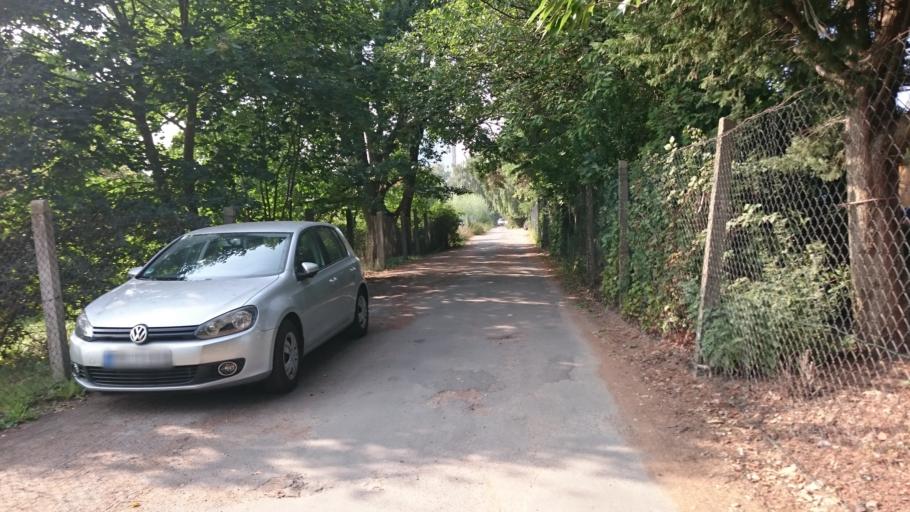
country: DE
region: Mecklenburg-Vorpommern
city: Rostock
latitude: 54.0797
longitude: 12.1182
